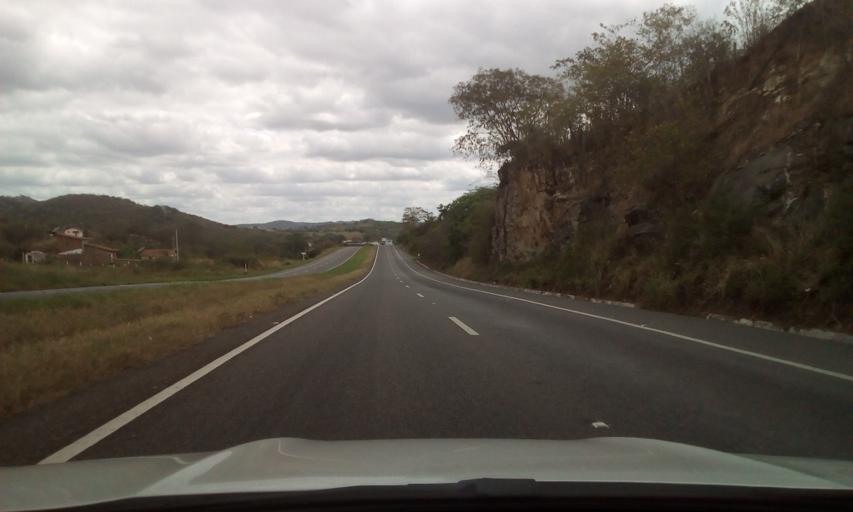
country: BR
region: Paraiba
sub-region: Massaranduba
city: Massaranduba
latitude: -7.2702
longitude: -35.7226
